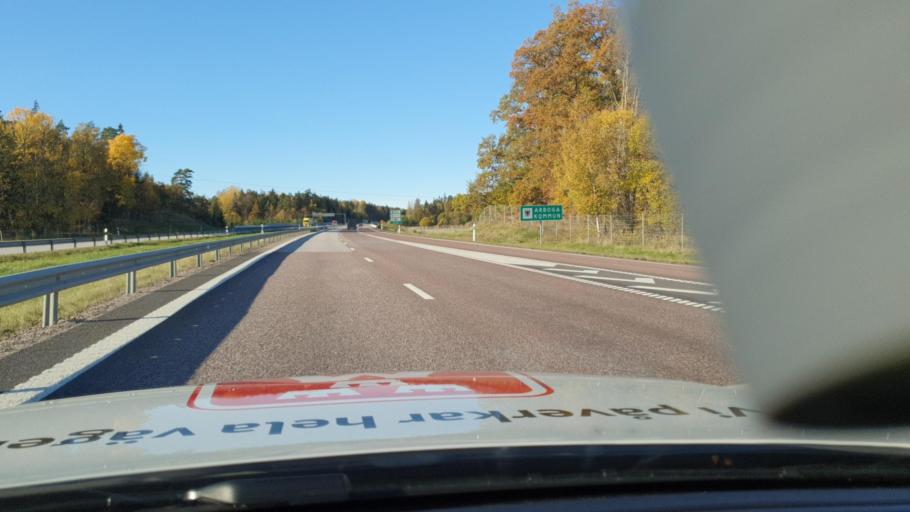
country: SE
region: Vaestmanland
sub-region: Arboga Kommun
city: Arboga
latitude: 59.4275
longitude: 15.8752
